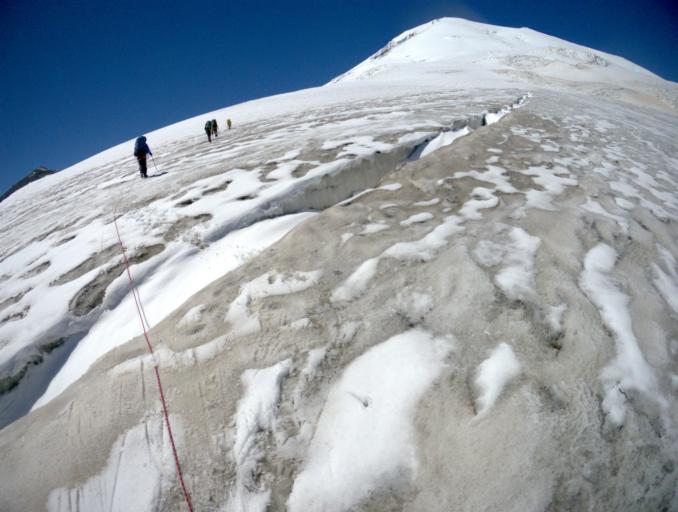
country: RU
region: Kabardino-Balkariya
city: Terskol
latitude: 43.3527
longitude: 42.5041
